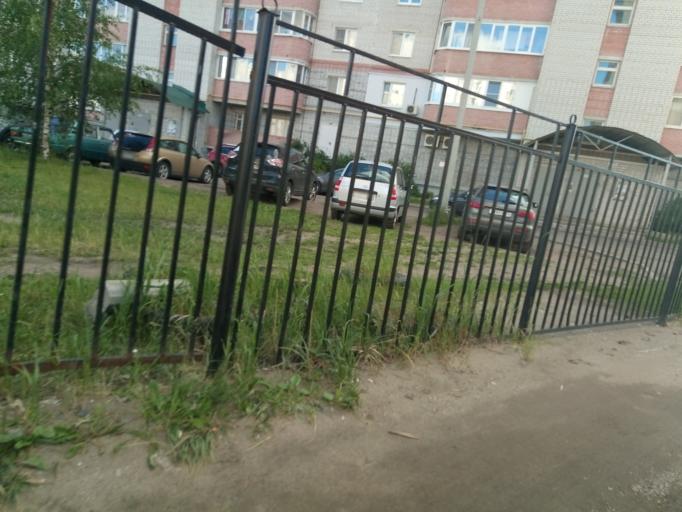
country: RU
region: Jaroslavl
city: Yaroslavl
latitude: 57.6395
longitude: 39.9495
